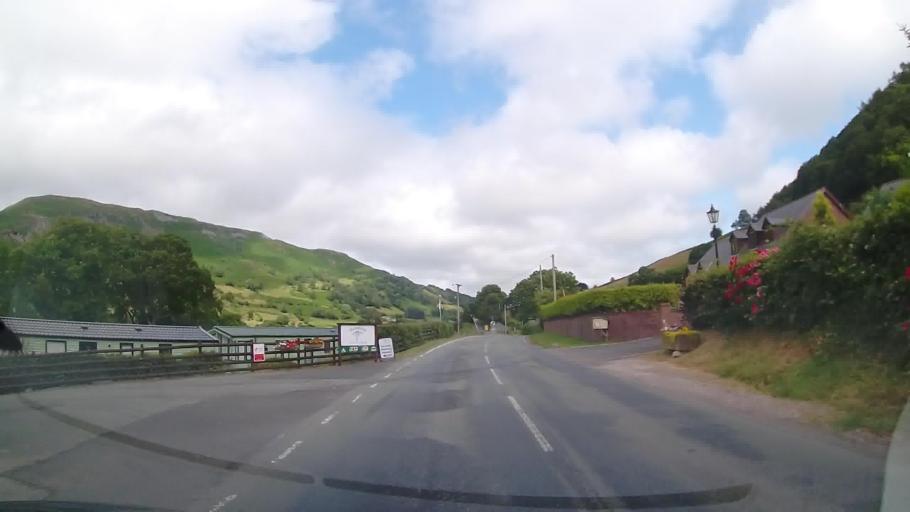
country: GB
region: Wales
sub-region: Sir Powys
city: Llangynog
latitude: 52.8229
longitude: -3.3963
